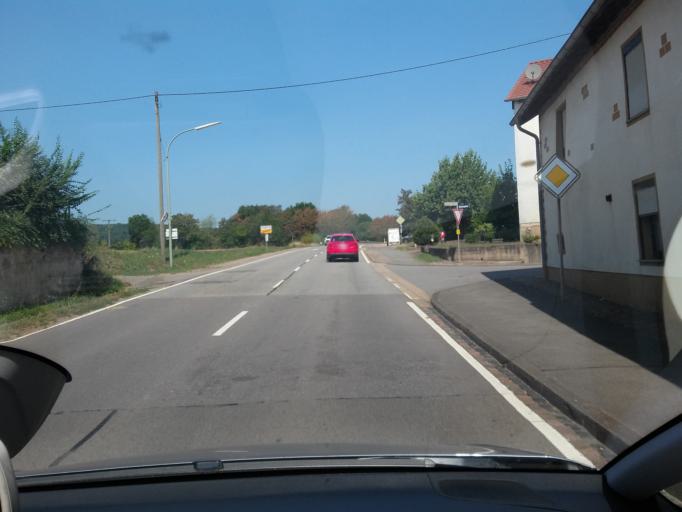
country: DE
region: Saarland
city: Mettlach
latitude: 49.4585
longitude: 6.5966
